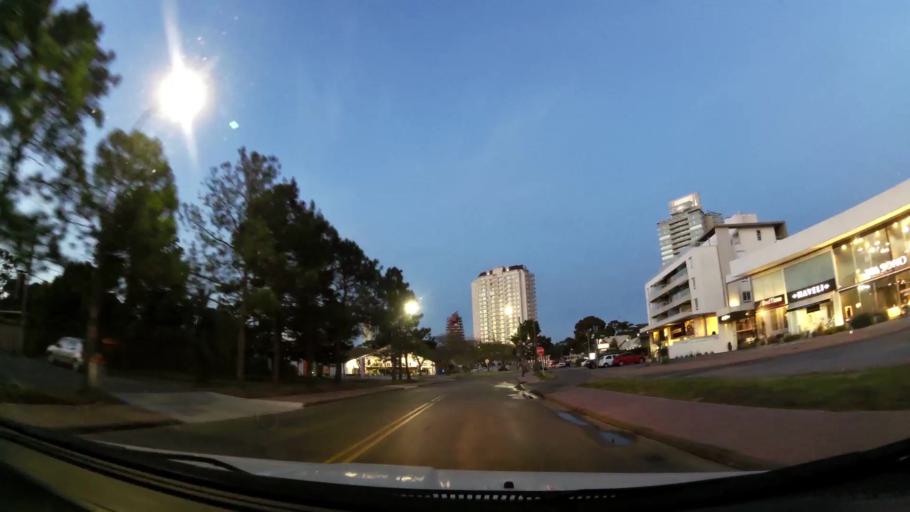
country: UY
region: Maldonado
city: Punta del Este
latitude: -34.9445
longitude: -54.9330
